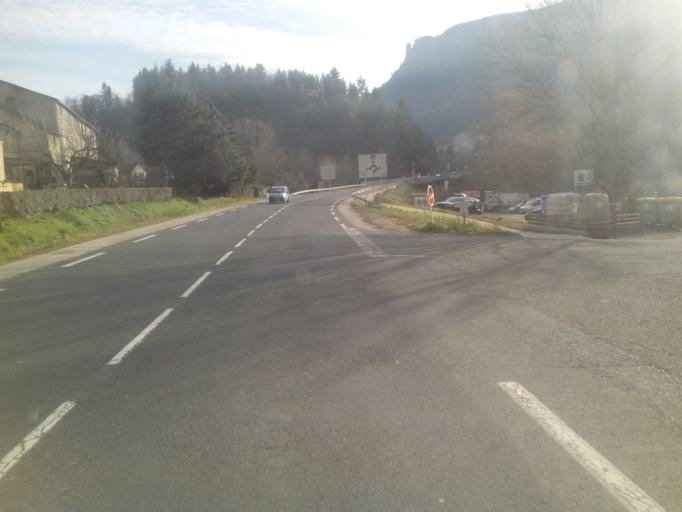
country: FR
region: Languedoc-Roussillon
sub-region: Departement de la Lozere
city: Florac
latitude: 44.3386
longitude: 3.5863
